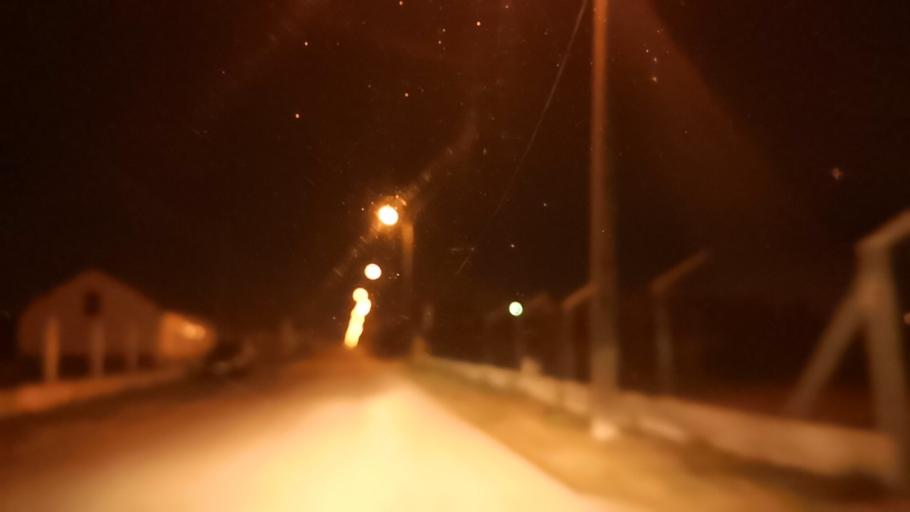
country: PT
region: Setubal
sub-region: Setubal
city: Setubal
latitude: 38.5212
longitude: -8.7976
